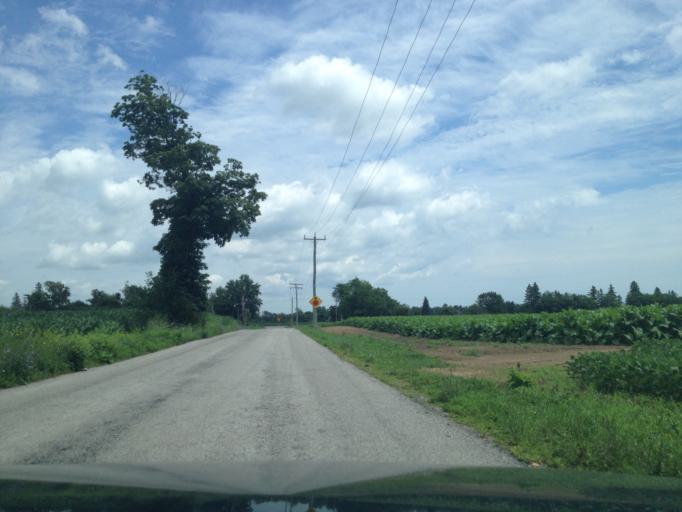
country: CA
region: Ontario
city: Norfolk County
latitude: 42.7824
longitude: -80.2874
